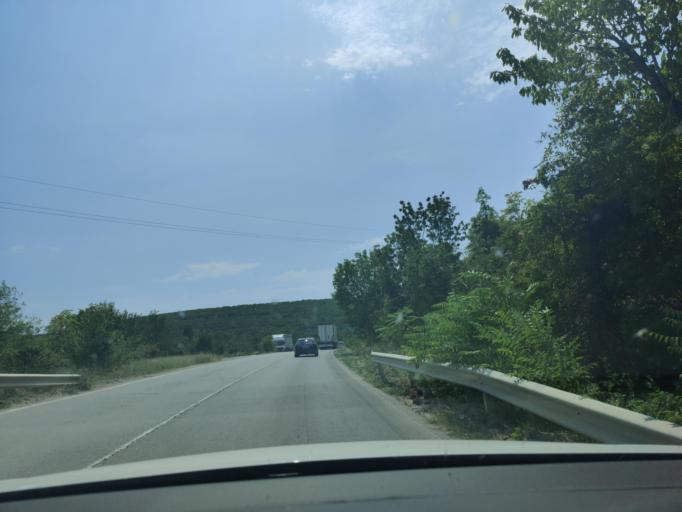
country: BG
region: Montana
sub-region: Obshtina Montana
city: Montana
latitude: 43.4318
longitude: 23.1241
